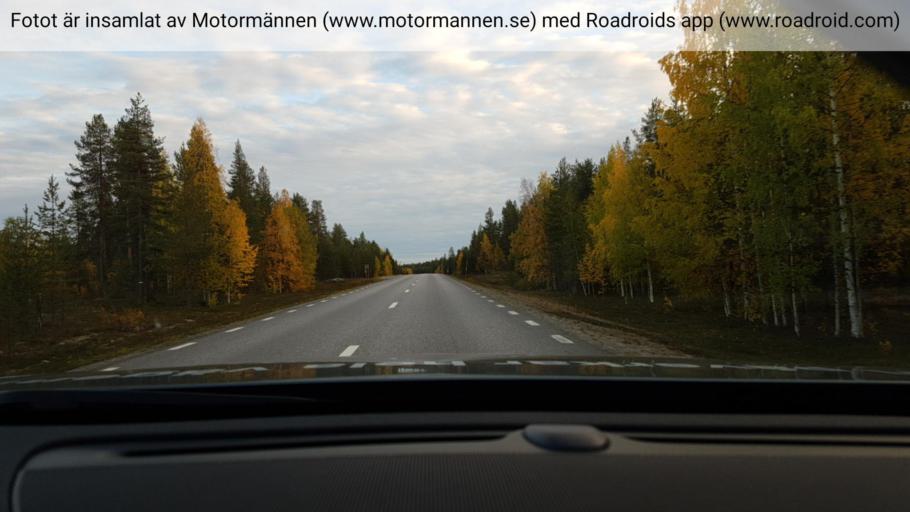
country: SE
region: Norrbotten
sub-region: Jokkmokks Kommun
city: Jokkmokk
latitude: 66.4099
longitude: 19.6893
